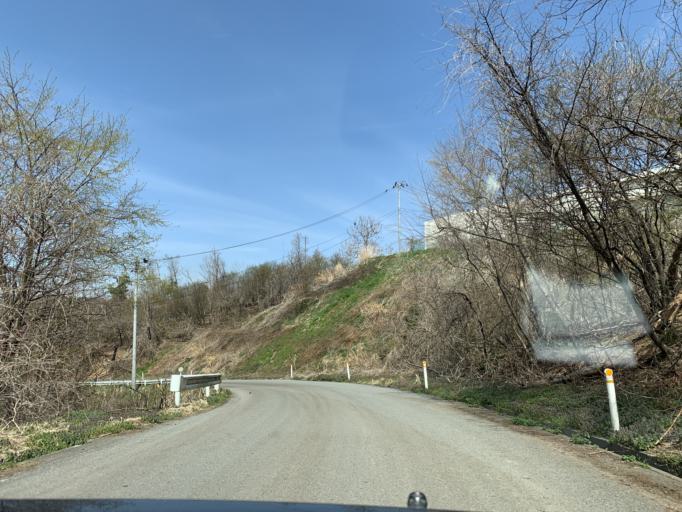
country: JP
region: Iwate
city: Ichinoseki
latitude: 38.8022
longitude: 141.2695
